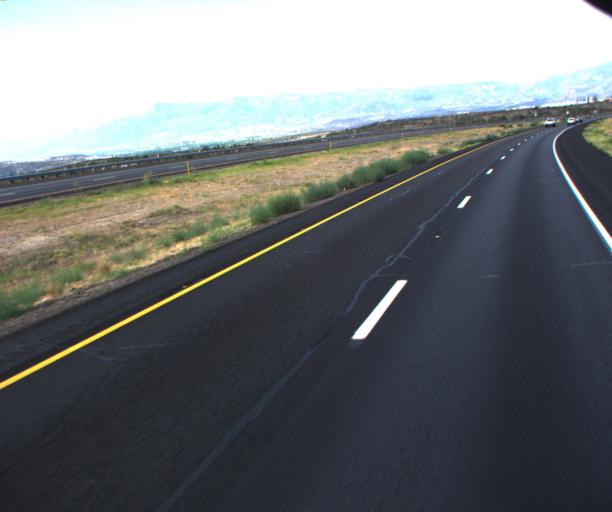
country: US
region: Arizona
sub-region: Yavapai County
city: Camp Verde
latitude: 34.6168
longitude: -111.8479
